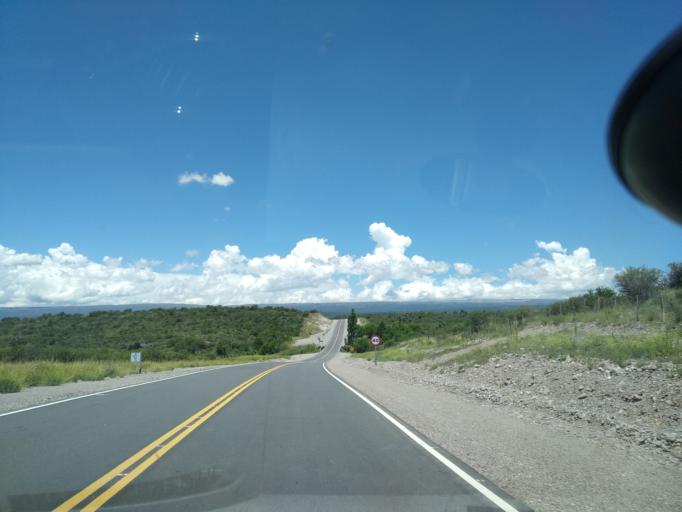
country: AR
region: Cordoba
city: Salsacate
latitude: -31.3459
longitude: -65.0916
